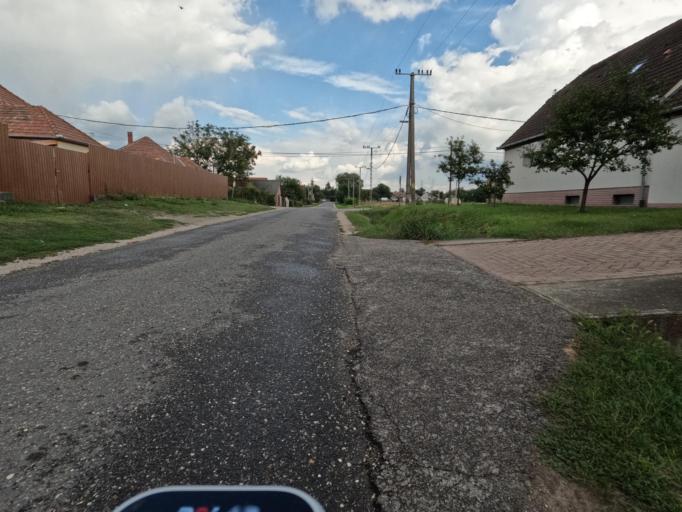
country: HU
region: Tolna
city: Tengelic
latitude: 46.5226
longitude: 18.7098
